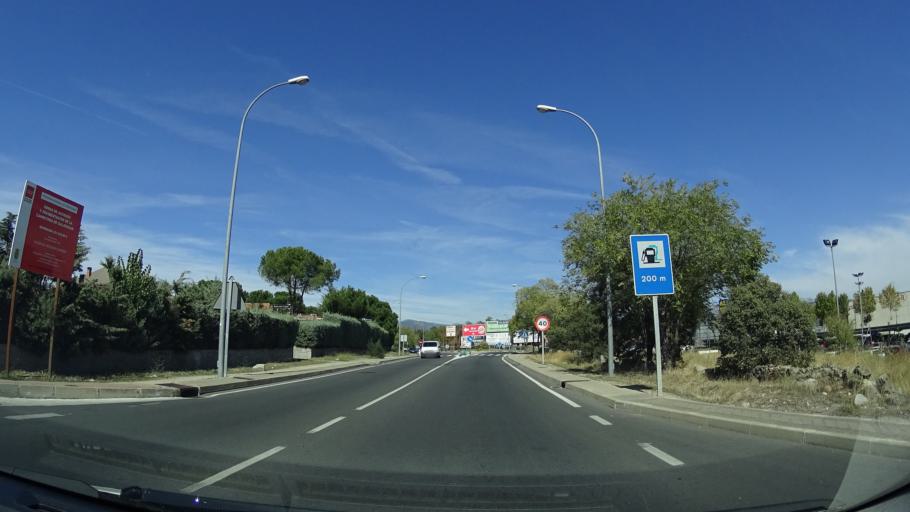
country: ES
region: Madrid
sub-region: Provincia de Madrid
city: Collado-Villalba
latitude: 40.6239
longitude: -4.0266
